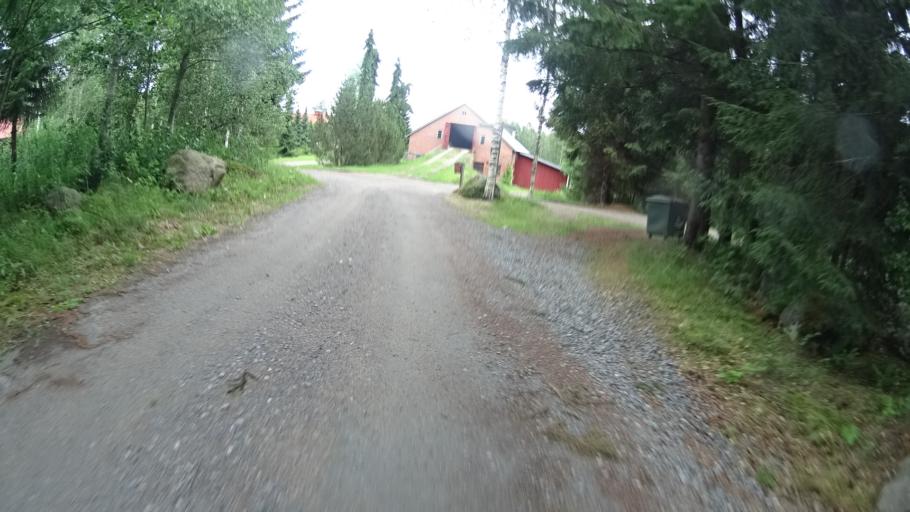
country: FI
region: Uusimaa
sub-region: Helsinki
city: Karkkila
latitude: 60.5803
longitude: 24.2911
